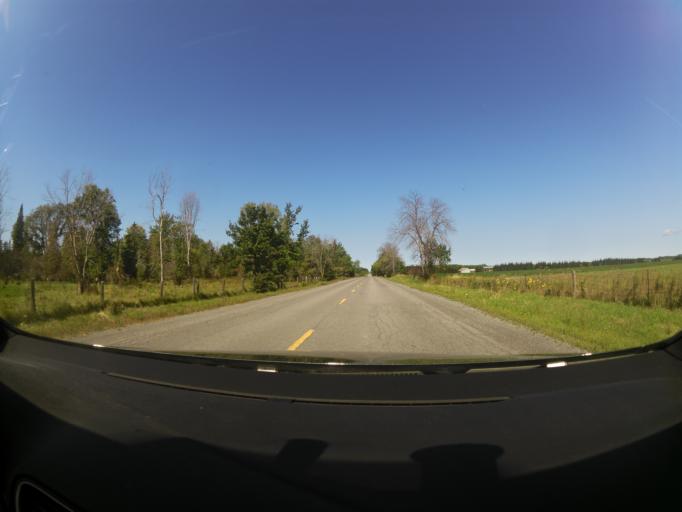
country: CA
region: Ontario
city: Arnprior
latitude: 45.3727
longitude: -76.2598
